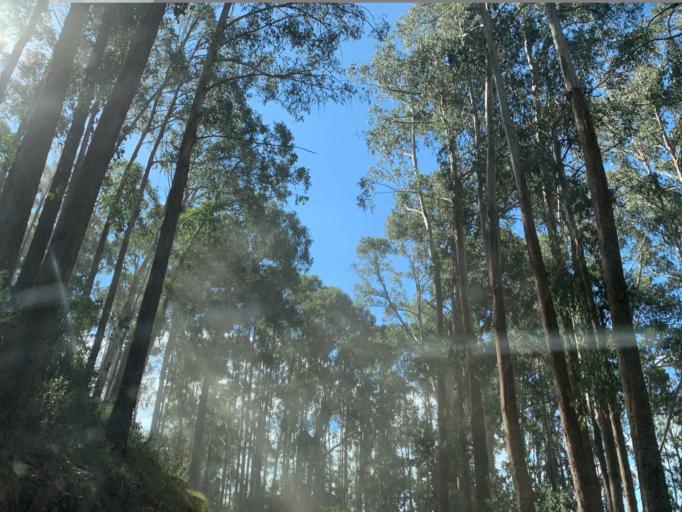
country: AU
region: Victoria
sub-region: Mansfield
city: Mansfield
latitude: -37.0973
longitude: 146.4667
